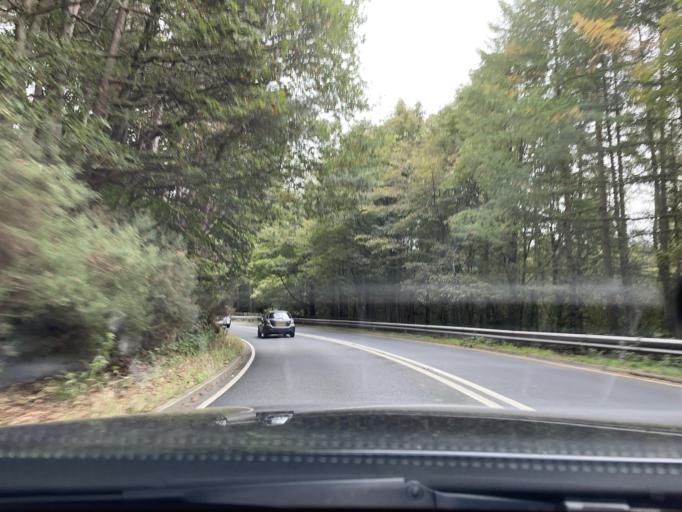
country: GB
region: England
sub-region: Sheffield
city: Bradfield
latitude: 53.3813
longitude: -1.5982
